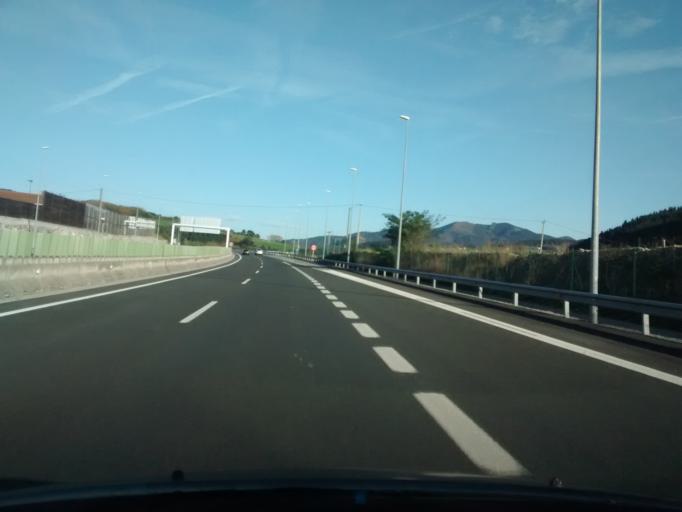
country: ES
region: Basque Country
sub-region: Bizkaia
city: Abadino
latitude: 43.1677
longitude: -2.5960
